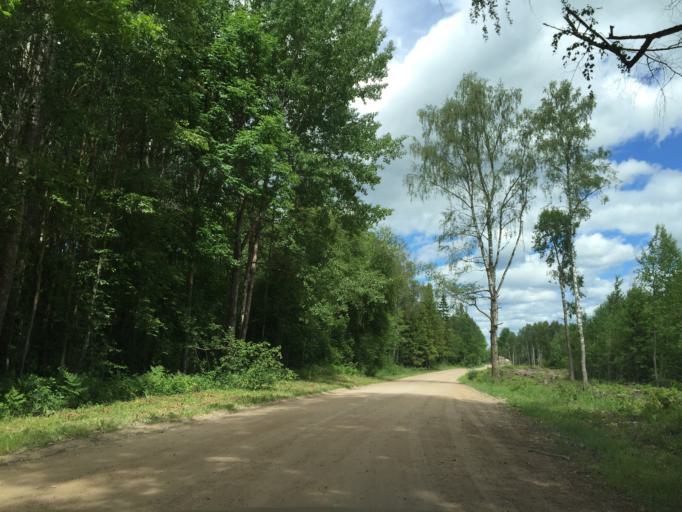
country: LV
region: Lecava
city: Iecava
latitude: 56.5679
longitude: 24.1086
